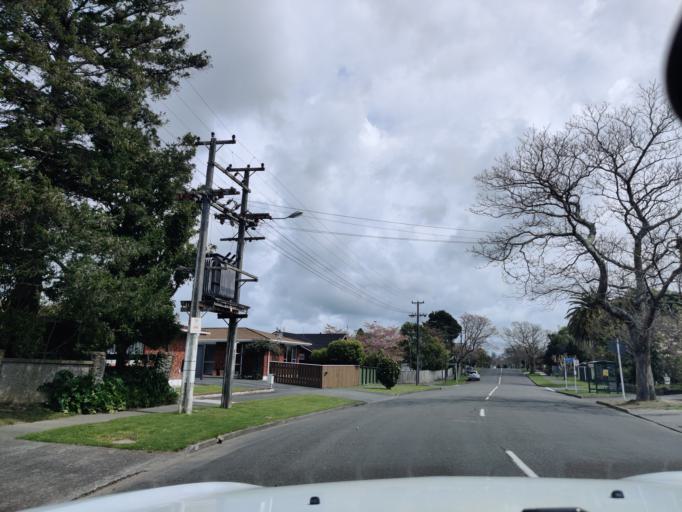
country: NZ
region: Manawatu-Wanganui
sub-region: Palmerston North City
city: Palmerston North
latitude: -40.3791
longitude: 175.5937
